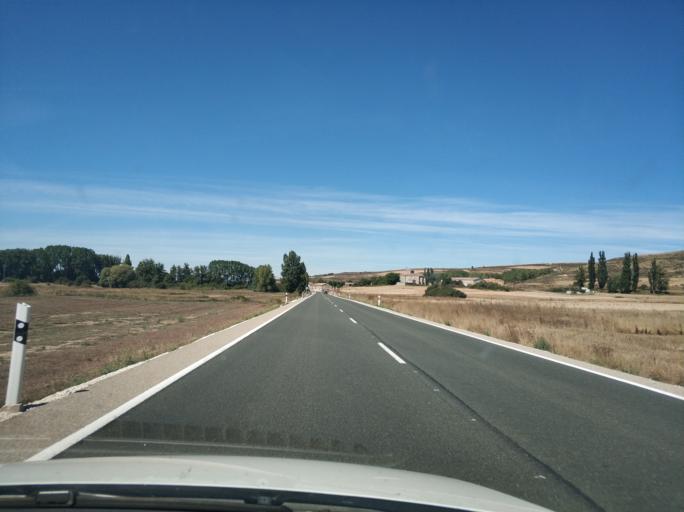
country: ES
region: Castille and Leon
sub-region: Provincia de Burgos
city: Tubilla del Agua
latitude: 42.6431
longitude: -3.8791
